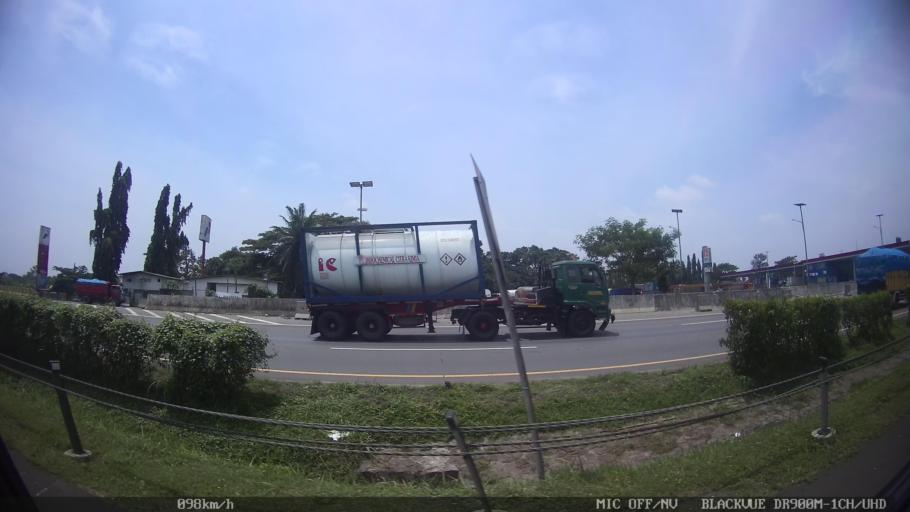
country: ID
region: West Java
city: Kresek
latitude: -6.1861
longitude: 106.4075
